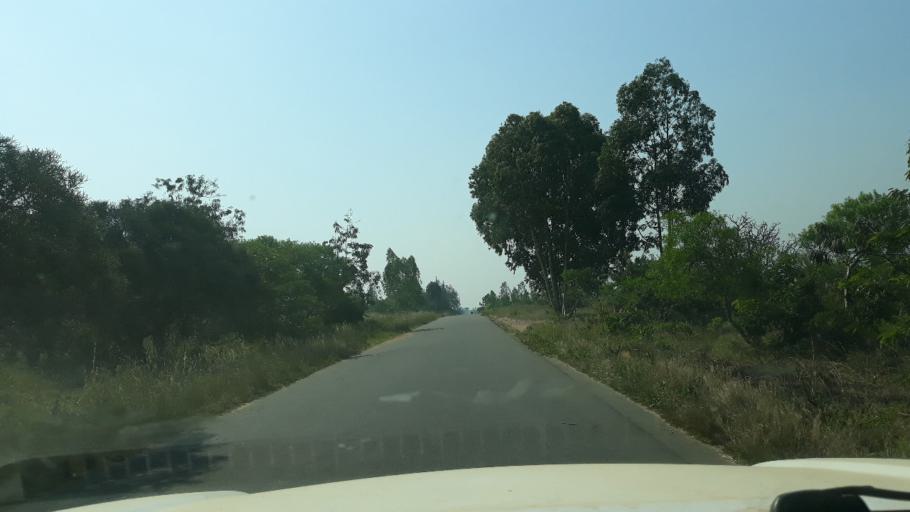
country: CD
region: South Kivu
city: Uvira
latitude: -3.2231
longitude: 29.1655
